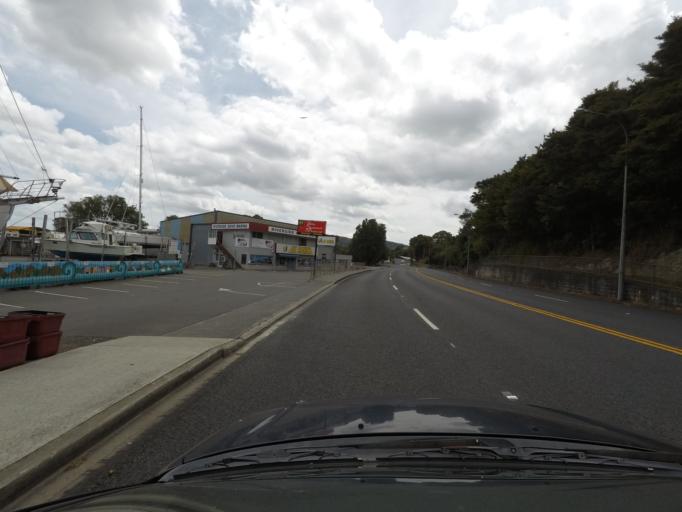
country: NZ
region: Northland
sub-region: Whangarei
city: Whangarei
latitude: -35.7274
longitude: 174.3341
